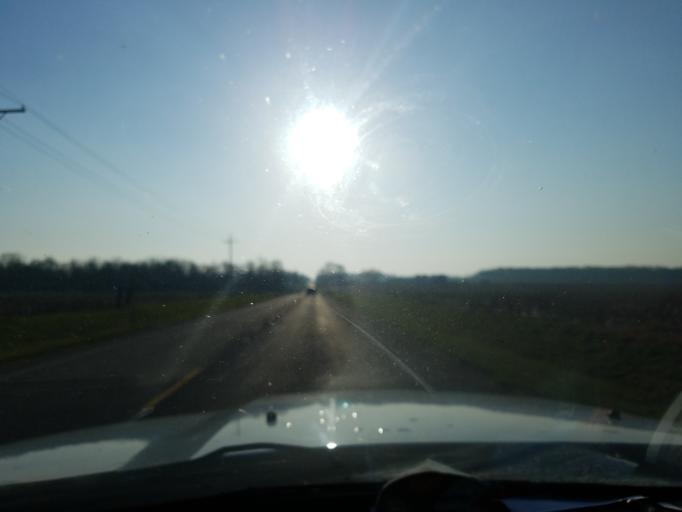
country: US
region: Indiana
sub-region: Vigo County
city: Seelyville
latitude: 39.3903
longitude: -87.2866
